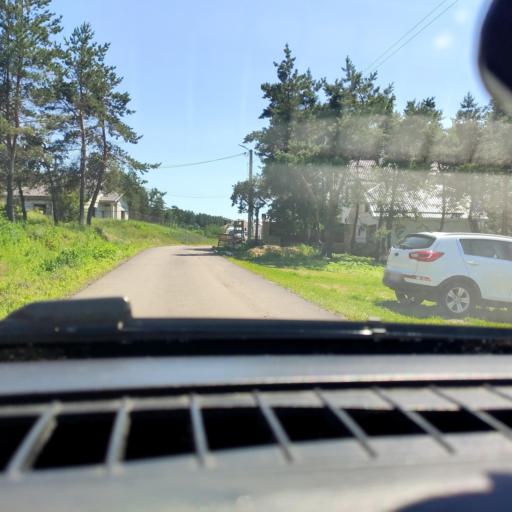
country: RU
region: Voronezj
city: Podgornoye
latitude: 51.7962
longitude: 39.1360
